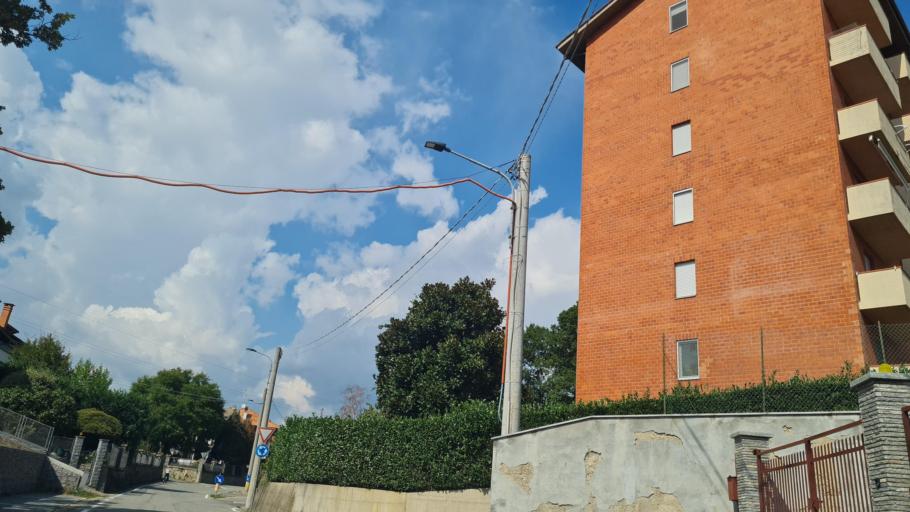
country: IT
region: Piedmont
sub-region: Provincia di Biella
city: Lessona
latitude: 45.5845
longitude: 8.1826
